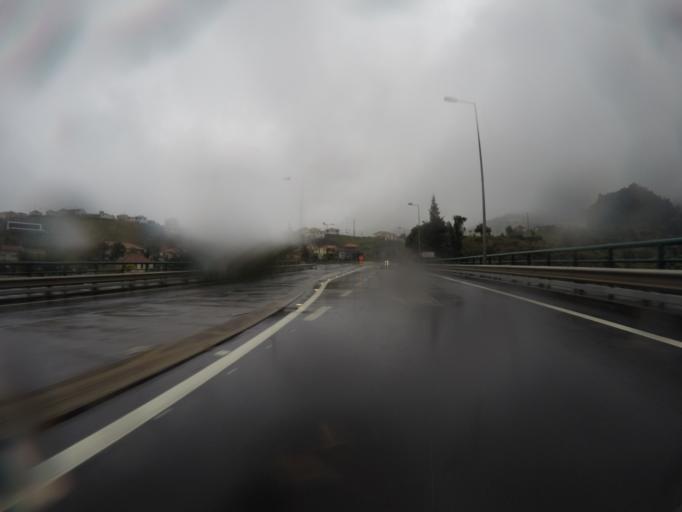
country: PT
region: Madeira
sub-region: Santana
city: Santana
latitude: 32.7616
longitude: -16.8304
